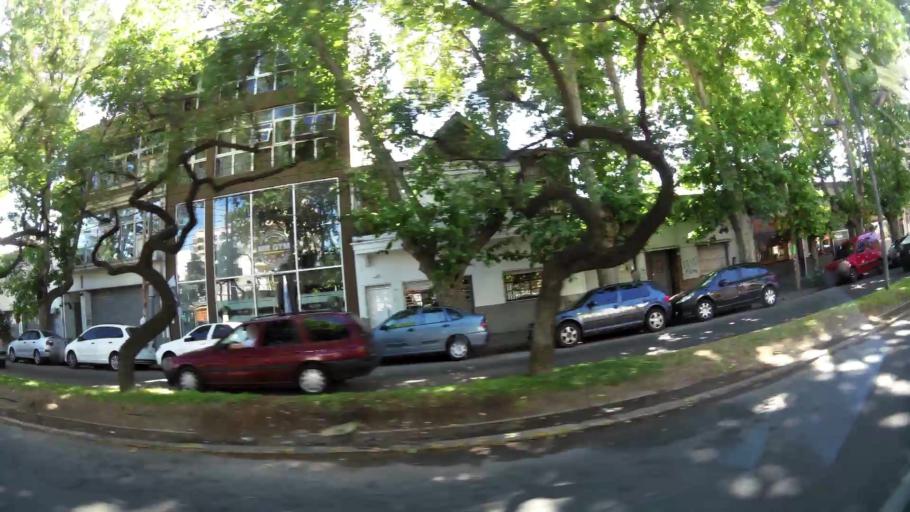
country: AR
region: Buenos Aires
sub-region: Partido de General San Martin
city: General San Martin
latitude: -34.5753
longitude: -58.5329
